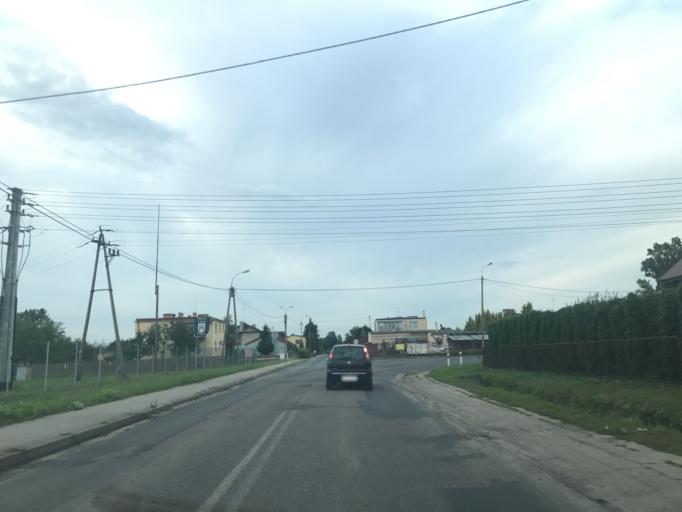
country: PL
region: Kujawsko-Pomorskie
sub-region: Powiat lipnowski
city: Lipno
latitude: 52.8551
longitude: 19.1758
